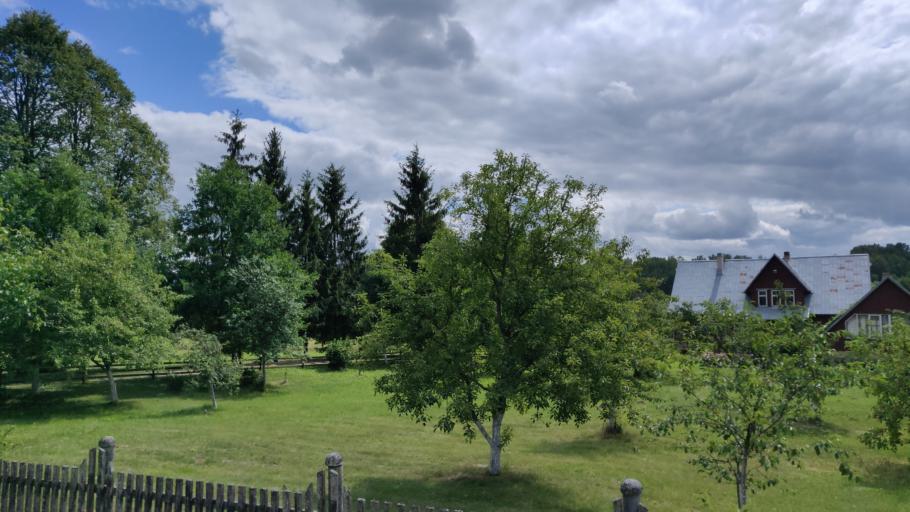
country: LT
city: Ariogala
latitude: 55.3661
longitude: 23.3212
